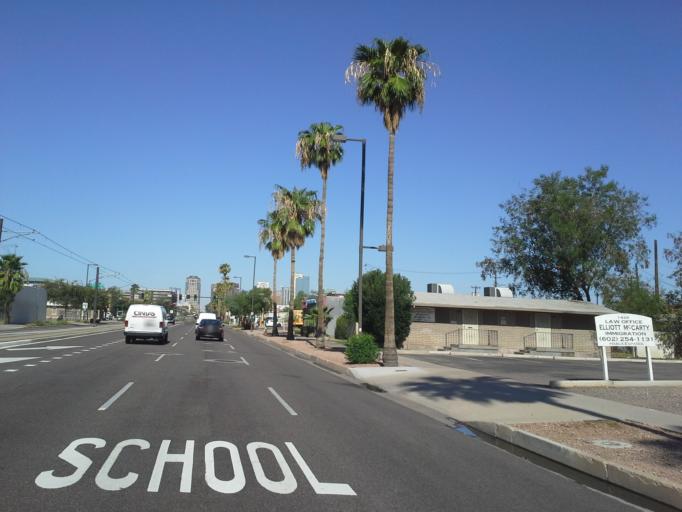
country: US
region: Arizona
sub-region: Maricopa County
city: Phoenix
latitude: 33.4484
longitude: -112.0505
